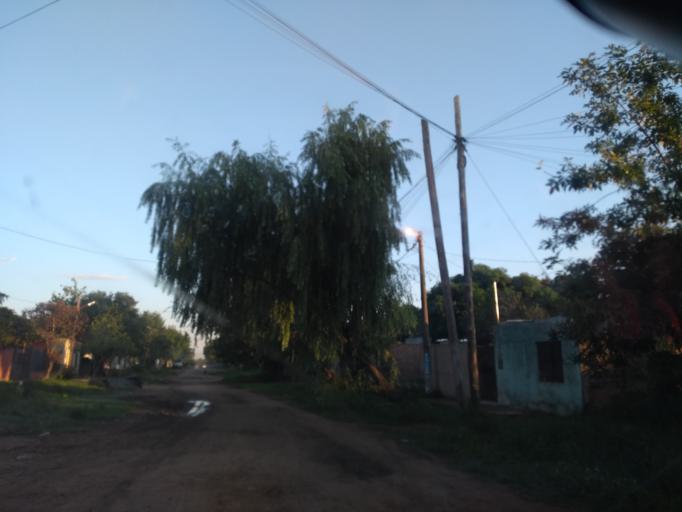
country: AR
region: Chaco
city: Resistencia
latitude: -27.4548
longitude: -58.9663
